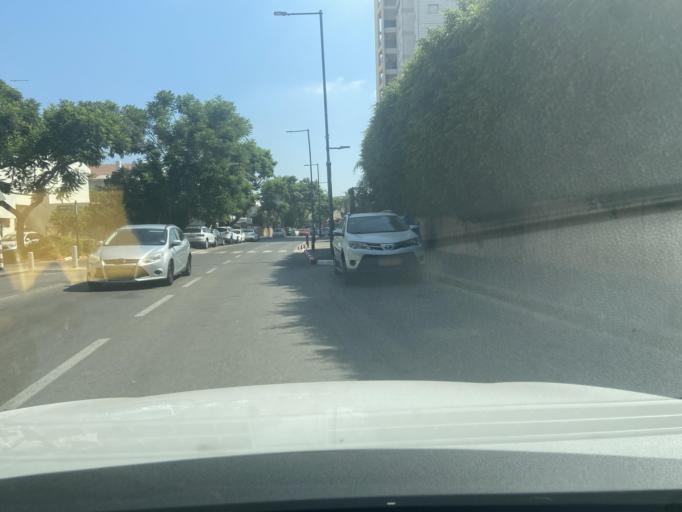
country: IL
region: Central District
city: Yehud
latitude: 32.0338
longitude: 34.8777
